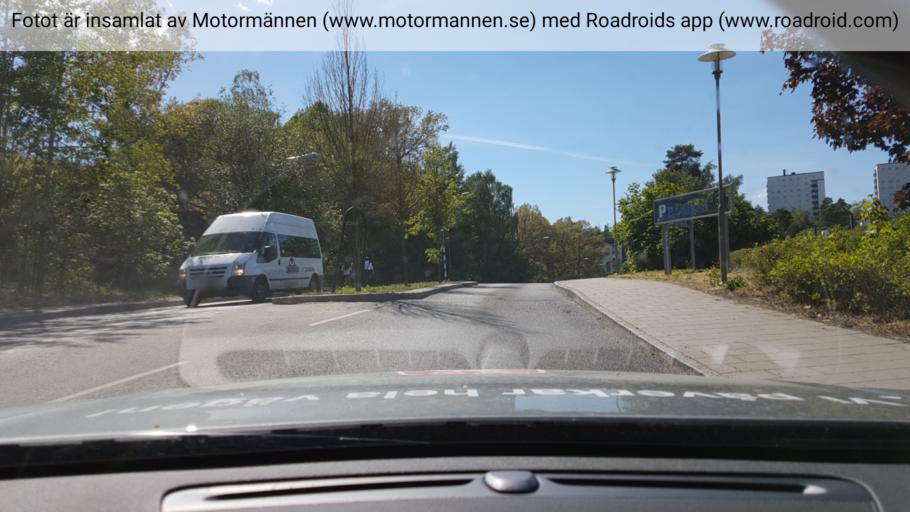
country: SE
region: Stockholm
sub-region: Stockholms Kommun
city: Arsta
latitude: 59.2565
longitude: 18.0269
